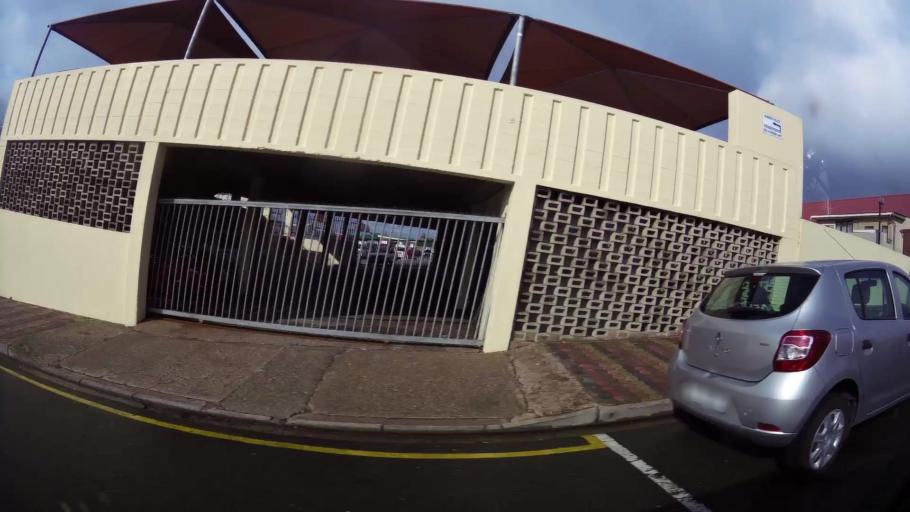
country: ZA
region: Western Cape
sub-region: Eden District Municipality
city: Mossel Bay
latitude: -34.1833
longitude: 22.1428
